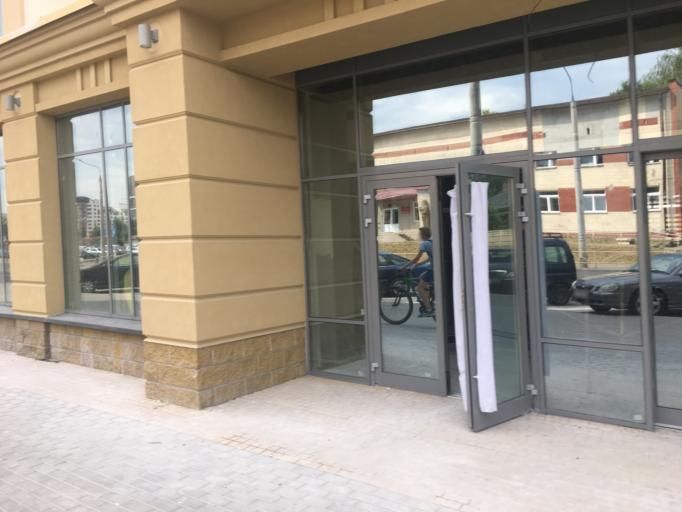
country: BY
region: Grodnenskaya
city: Hrodna
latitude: 53.6809
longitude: 23.8430
